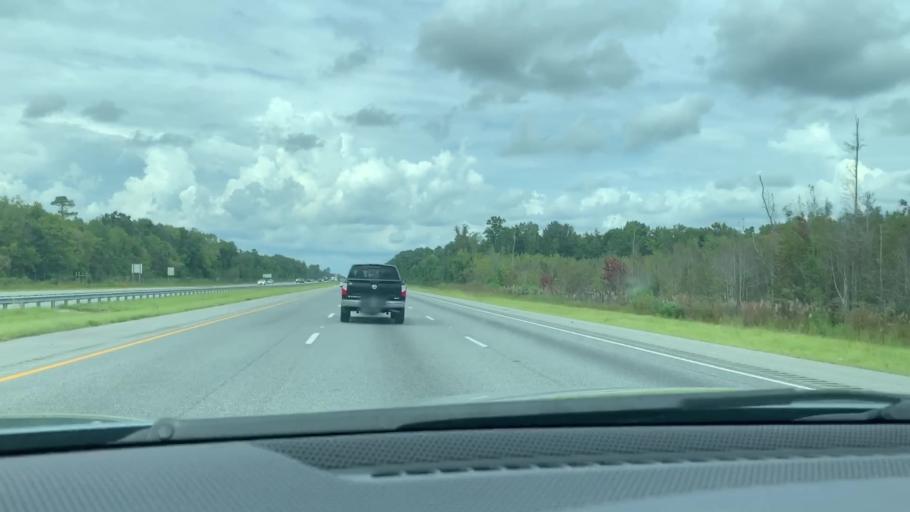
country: US
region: Georgia
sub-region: McIntosh County
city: Darien
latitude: 31.4971
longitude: -81.4464
